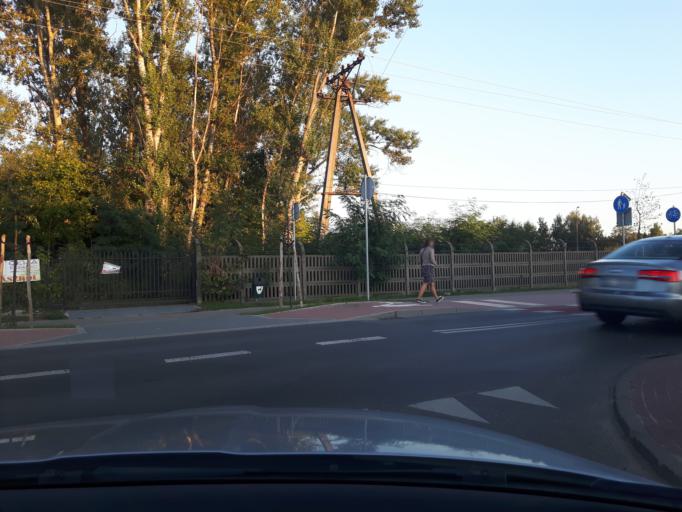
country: PL
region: Masovian Voivodeship
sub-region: Powiat wolominski
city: Kobylka
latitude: 52.3311
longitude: 21.1929
